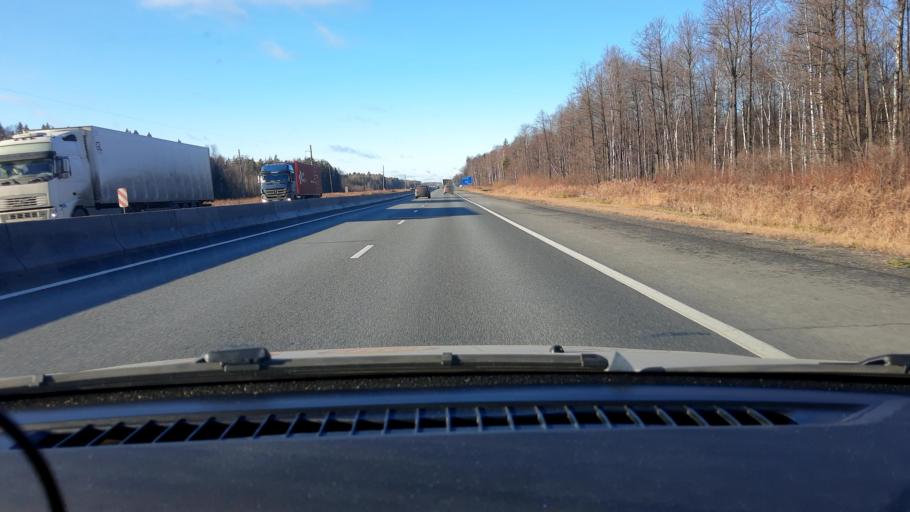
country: RU
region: Nizjnij Novgorod
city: Volodarsk
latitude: 56.2861
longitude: 43.1817
